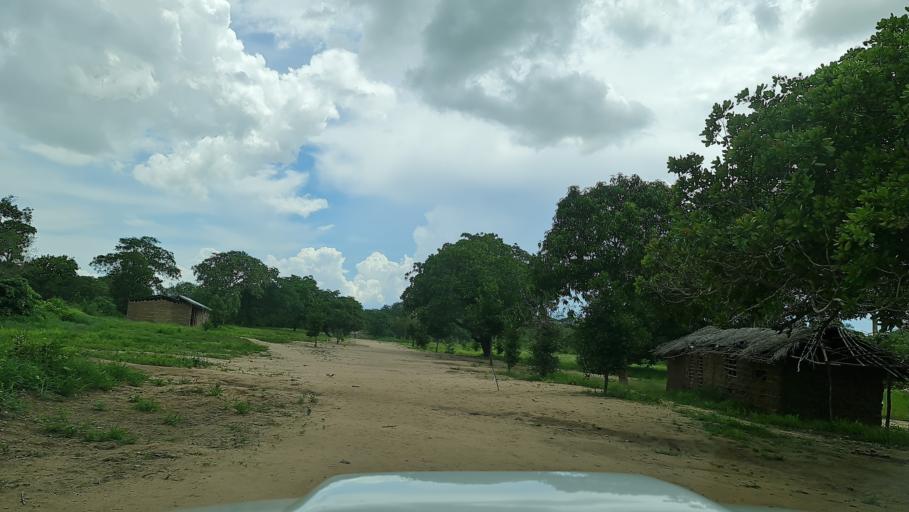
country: MZ
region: Nampula
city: Ilha de Mocambique
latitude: -15.4986
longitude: 40.1595
